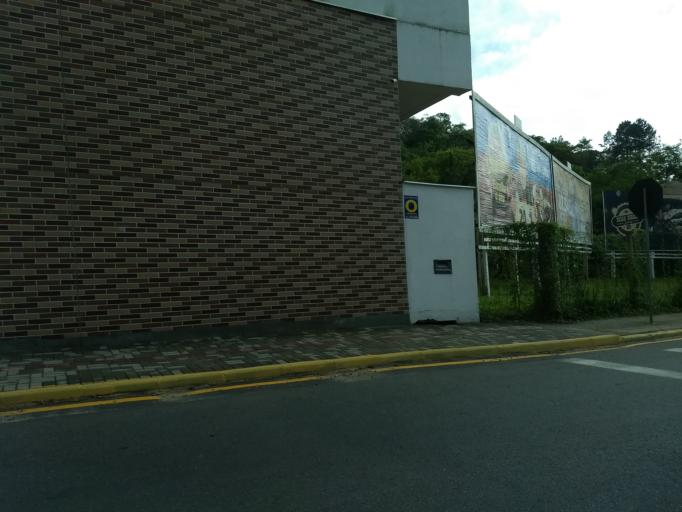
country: BR
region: Santa Catarina
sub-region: Jaragua Do Sul
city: Jaragua do Sul
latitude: -26.4818
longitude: -49.0785
